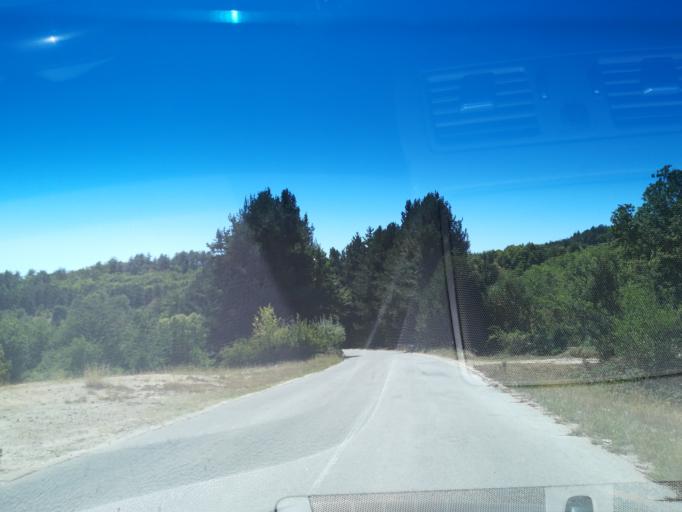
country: BG
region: Pazardzhik
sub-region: Obshtina Strelcha
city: Strelcha
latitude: 42.5439
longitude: 24.3305
